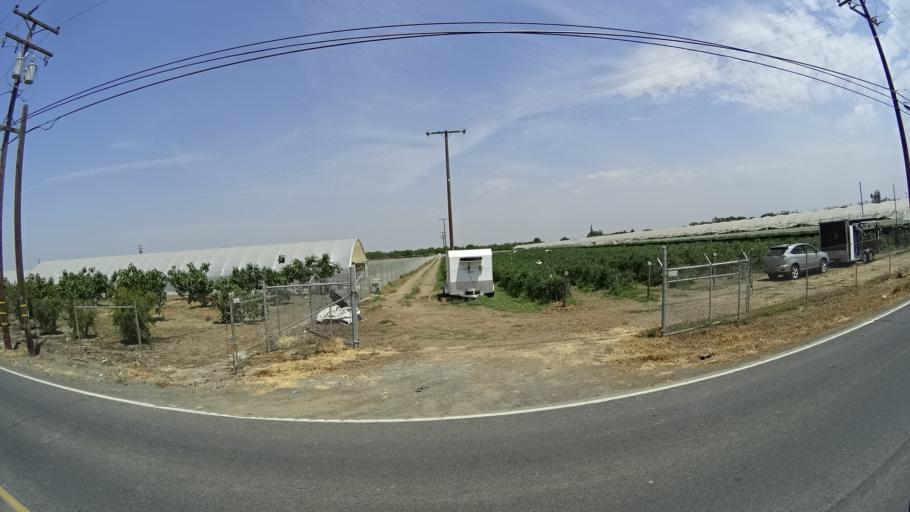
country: US
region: California
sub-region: Kings County
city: Armona
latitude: 36.3280
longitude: -119.7114
